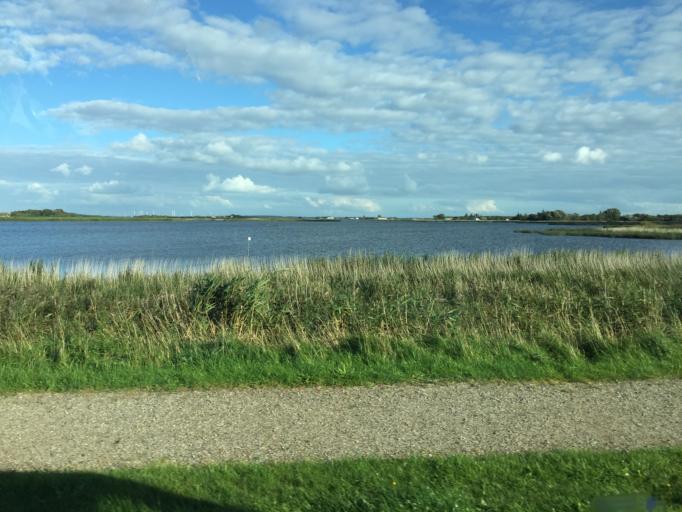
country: DE
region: Schleswig-Holstein
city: Neukirchen
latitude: 54.8974
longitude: 8.7506
